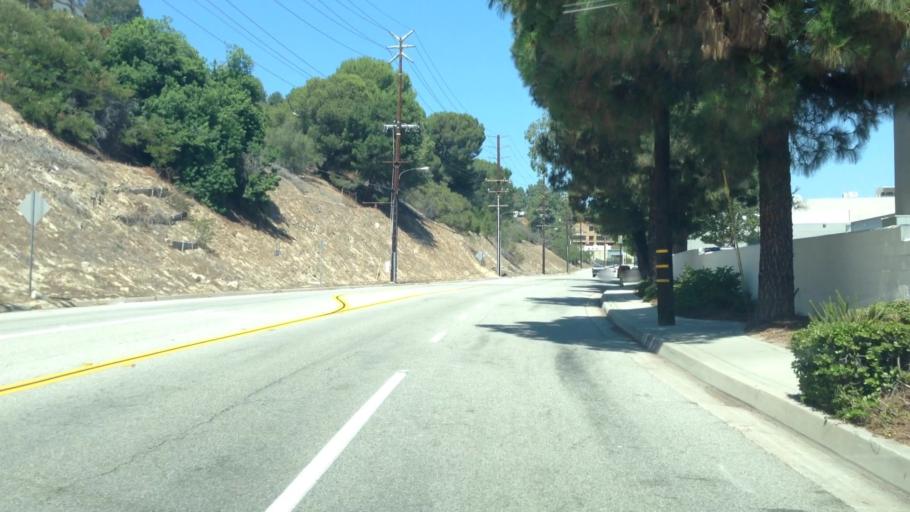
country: US
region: California
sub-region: Los Angeles County
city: Rolling Hills Estates
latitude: 33.7731
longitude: -118.3770
